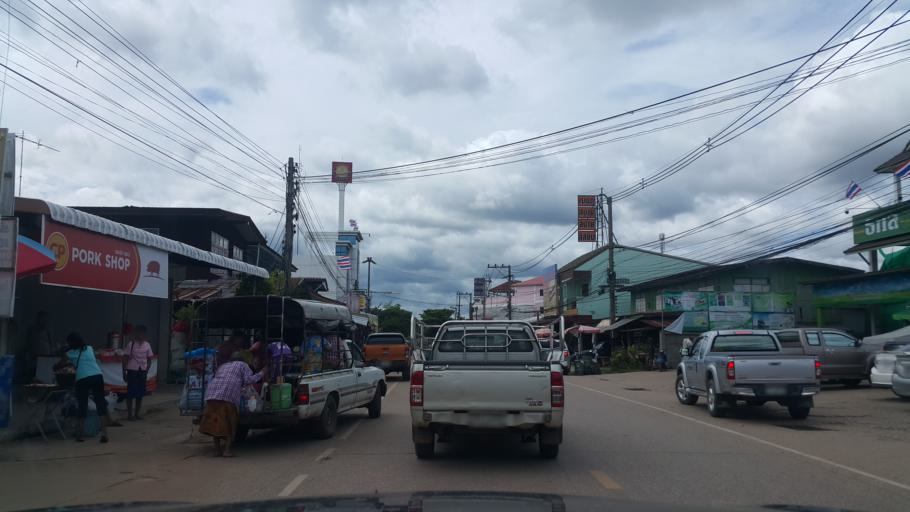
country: TH
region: Phitsanulok
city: Chat Trakan
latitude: 17.2726
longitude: 100.6064
